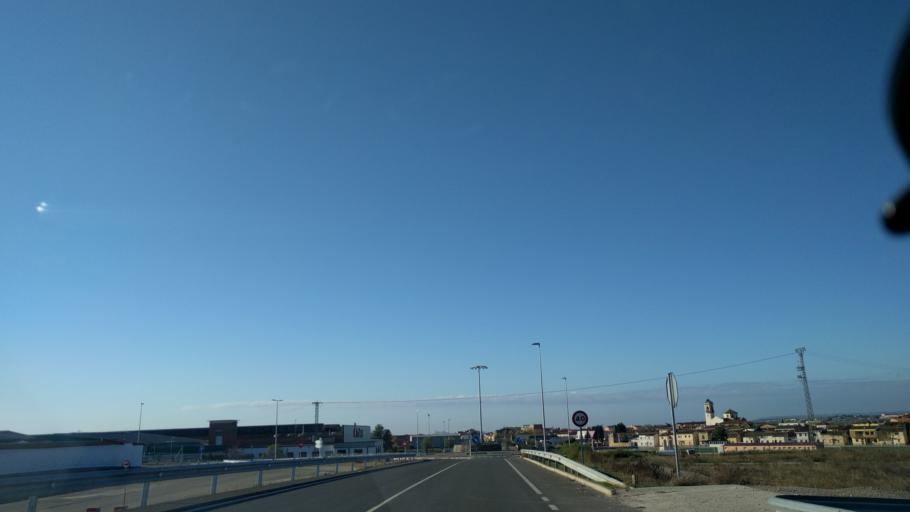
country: ES
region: Catalonia
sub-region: Provincia de Lleida
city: Corbins
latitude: 41.6928
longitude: 0.7349
